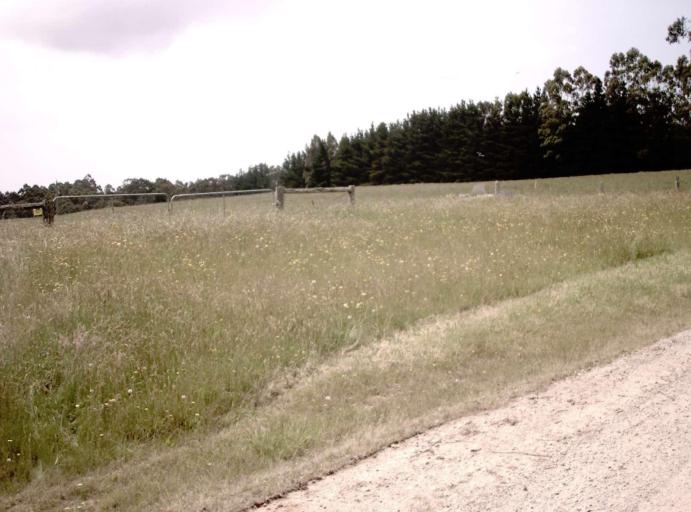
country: AU
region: Victoria
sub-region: Latrobe
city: Traralgon
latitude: -38.3792
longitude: 146.6687
